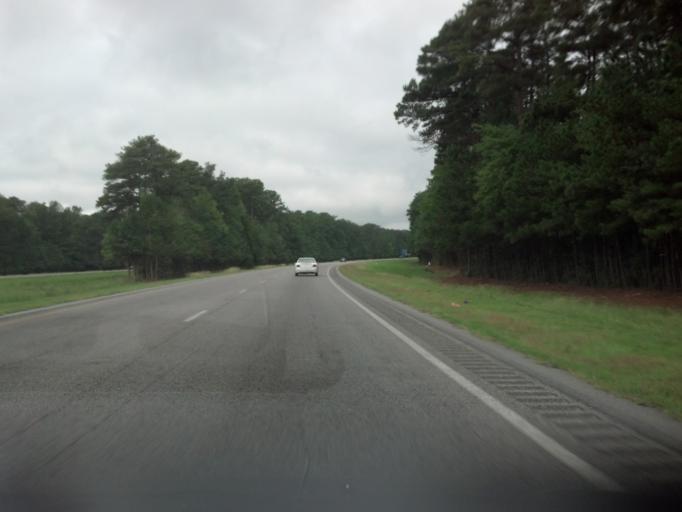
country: US
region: North Carolina
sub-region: Nash County
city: Rocky Mount
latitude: 35.9365
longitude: -77.7455
